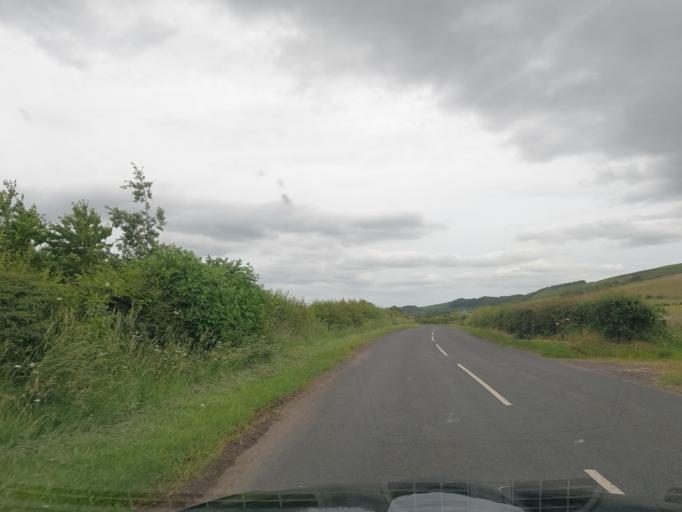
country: GB
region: England
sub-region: Northumberland
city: Wooler
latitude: 55.5514
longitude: -1.9974
